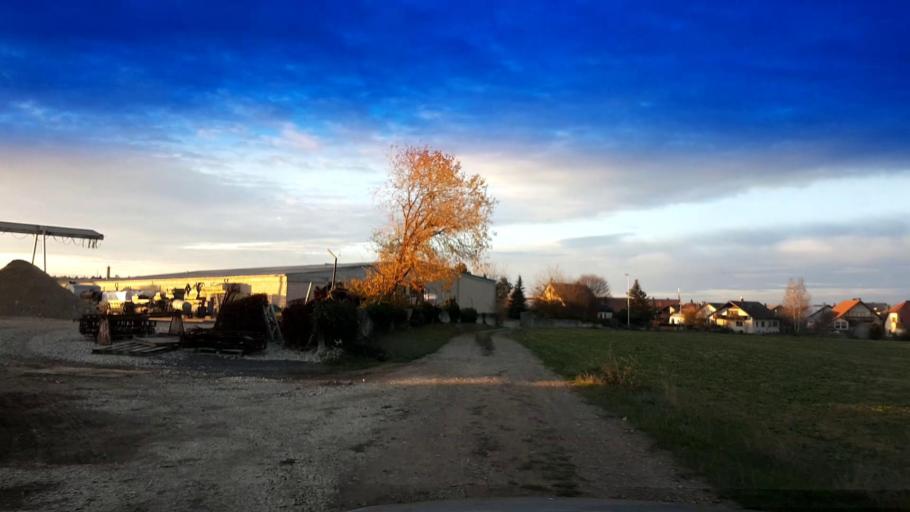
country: DE
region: Bavaria
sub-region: Upper Franconia
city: Priesendorf
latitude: 49.8780
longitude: 10.7327
